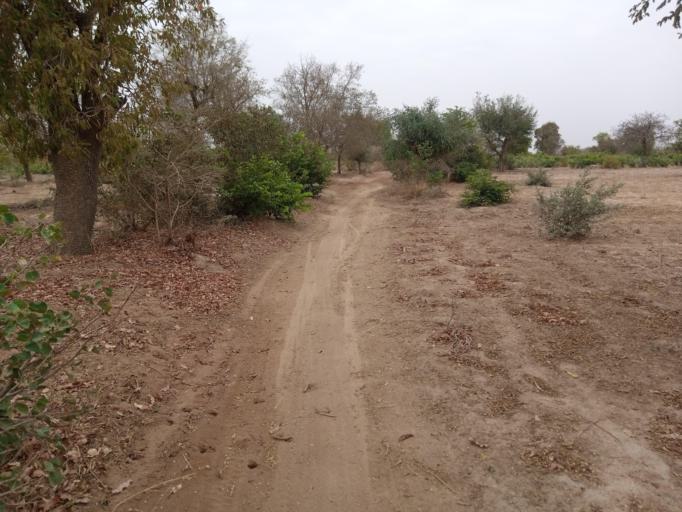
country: BF
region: Boucle du Mouhoun
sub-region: Province de la Kossi
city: Nouna
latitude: 12.8329
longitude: -4.0772
